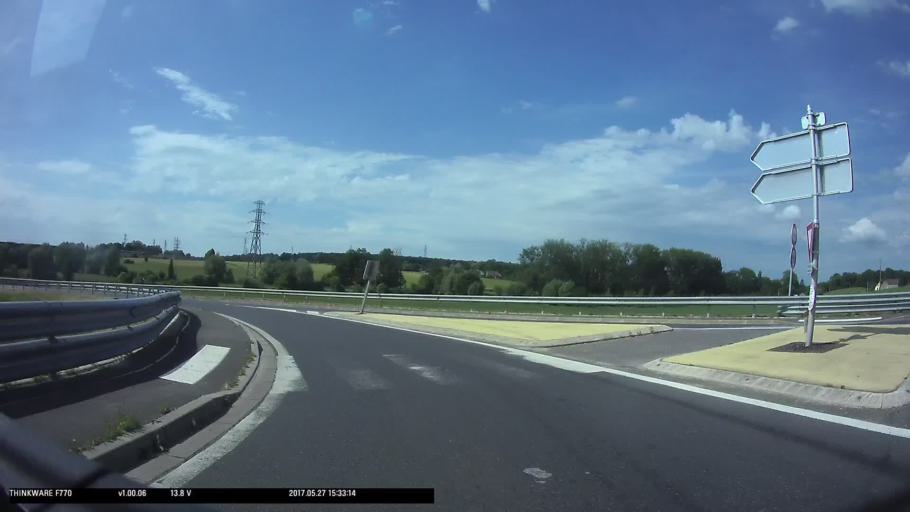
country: FR
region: Picardie
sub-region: Departement de l'Oise
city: Trie-Chateau
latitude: 49.2817
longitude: 1.8358
